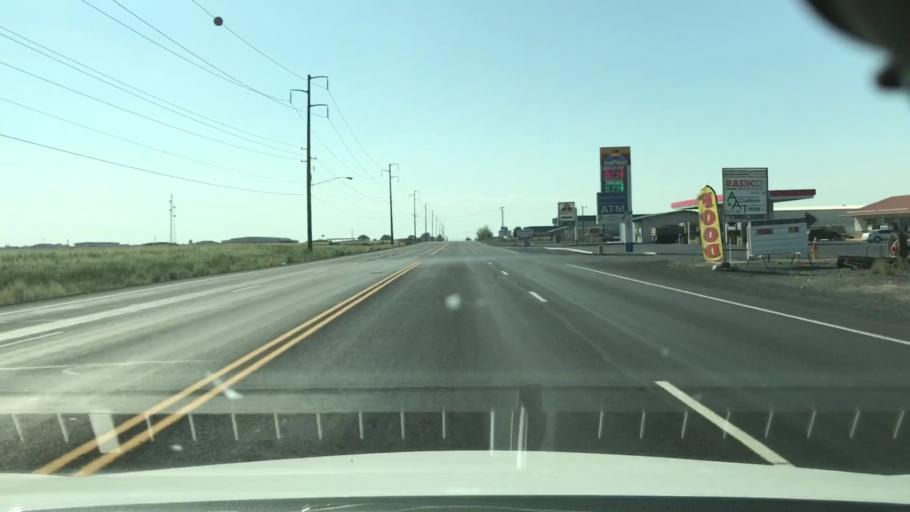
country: US
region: Washington
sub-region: Grant County
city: Moses Lake
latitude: 47.1310
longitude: -119.2377
